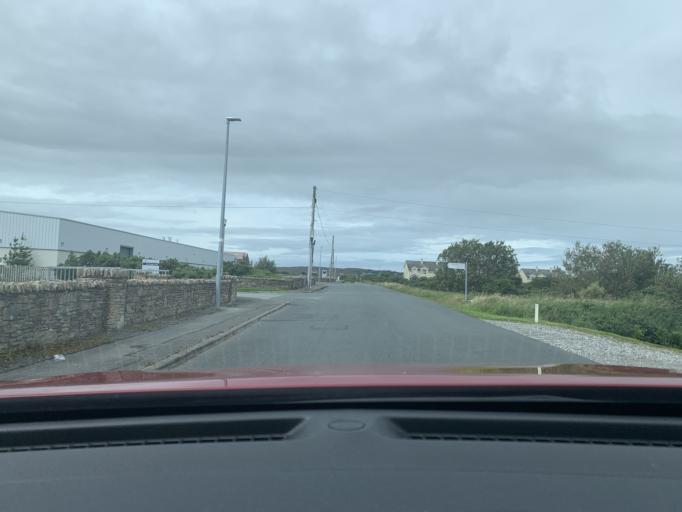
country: IE
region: Ulster
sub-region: County Donegal
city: Dungloe
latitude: 54.9569
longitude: -8.3711
